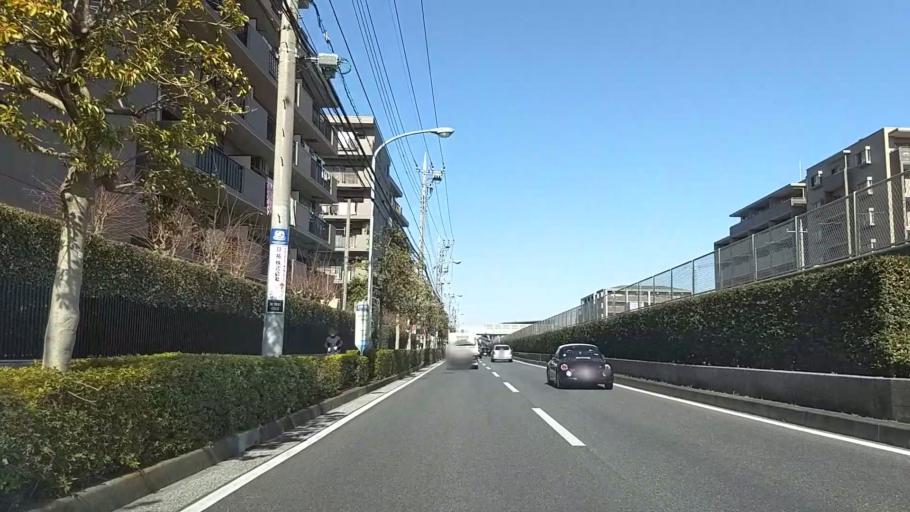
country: JP
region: Kanagawa
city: Yokohama
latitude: 35.5196
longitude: 139.6126
